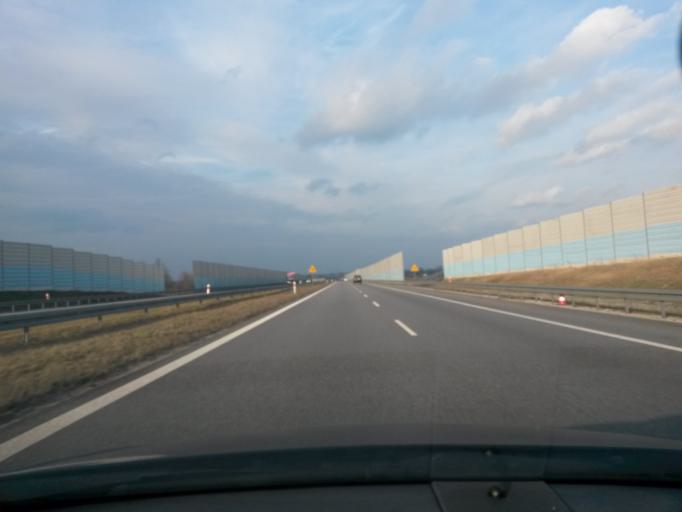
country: PL
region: Lodz Voivodeship
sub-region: powiat Lowicki
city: Lyszkowice
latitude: 51.9667
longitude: 19.8617
